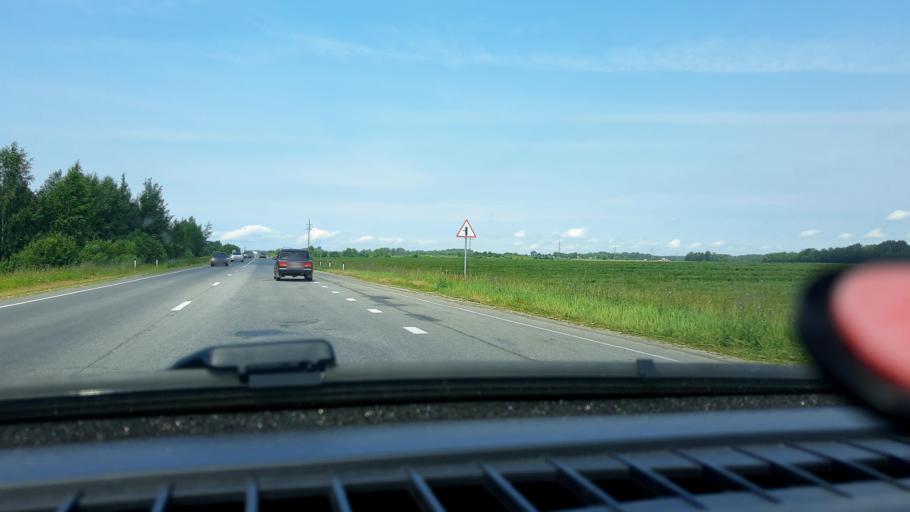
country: RU
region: Nizjnij Novgorod
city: Gorodets
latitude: 56.6640
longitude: 43.4947
